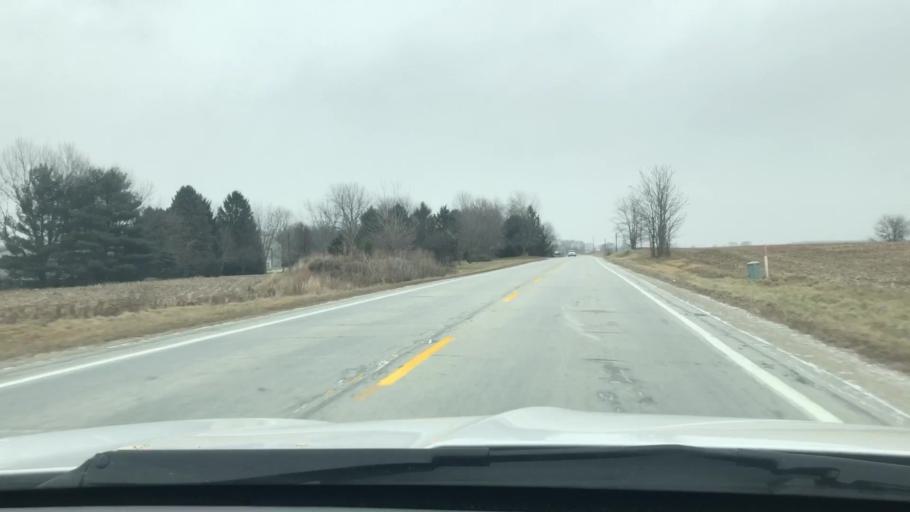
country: US
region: Indiana
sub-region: Fulton County
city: Akron
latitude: 41.0393
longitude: -86.0782
